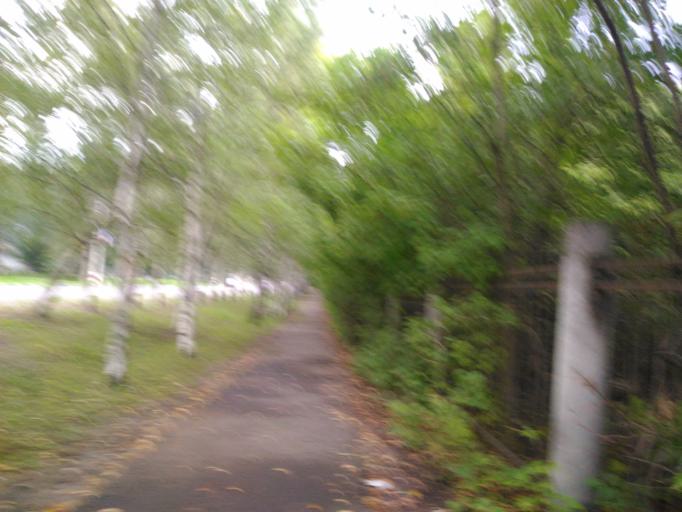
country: RU
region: Ulyanovsk
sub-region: Ulyanovskiy Rayon
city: Ulyanovsk
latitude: 54.2692
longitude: 48.3350
